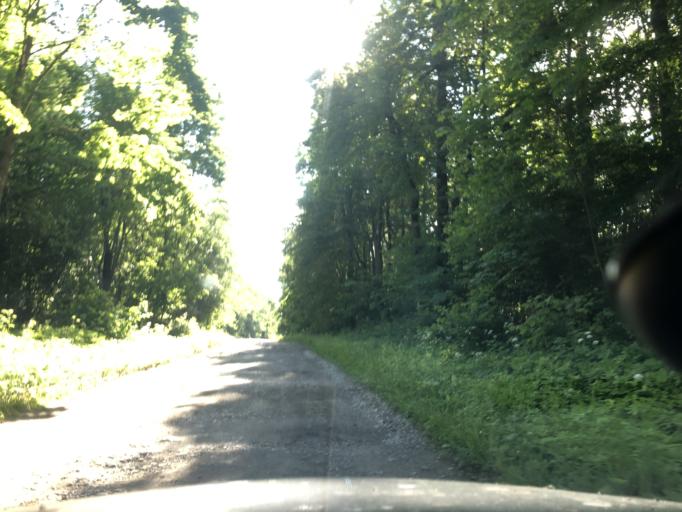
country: RU
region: Tula
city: Shvartsevskiy
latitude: 54.2562
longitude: 37.9180
